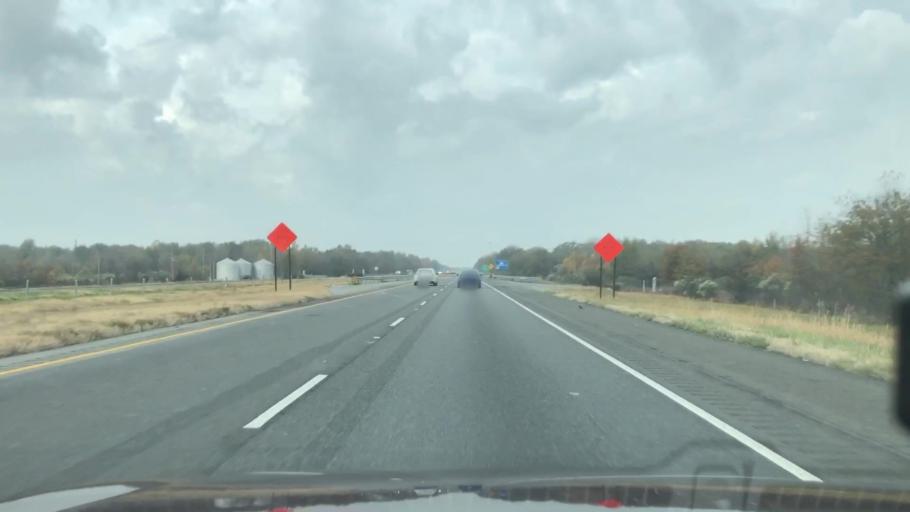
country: US
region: Louisiana
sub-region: Richland Parish
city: Delhi
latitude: 32.4387
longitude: -91.4663
